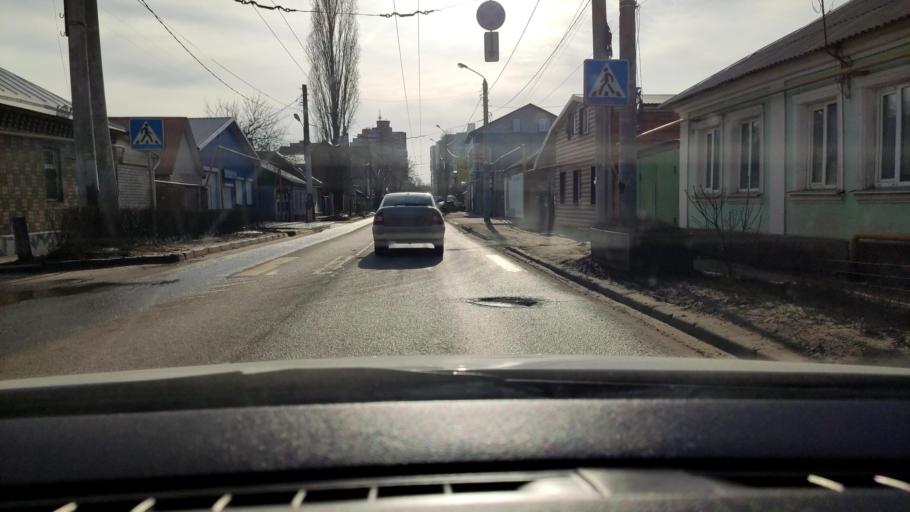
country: RU
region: Voronezj
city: Voronezh
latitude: 51.6666
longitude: 39.1662
